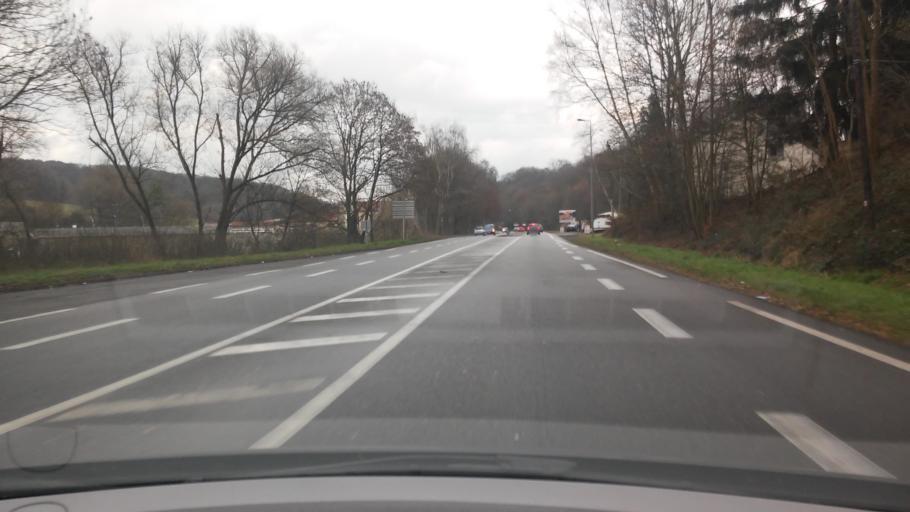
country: FR
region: Lorraine
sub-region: Departement de la Moselle
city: Saint-Avold
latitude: 49.1091
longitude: 6.7300
